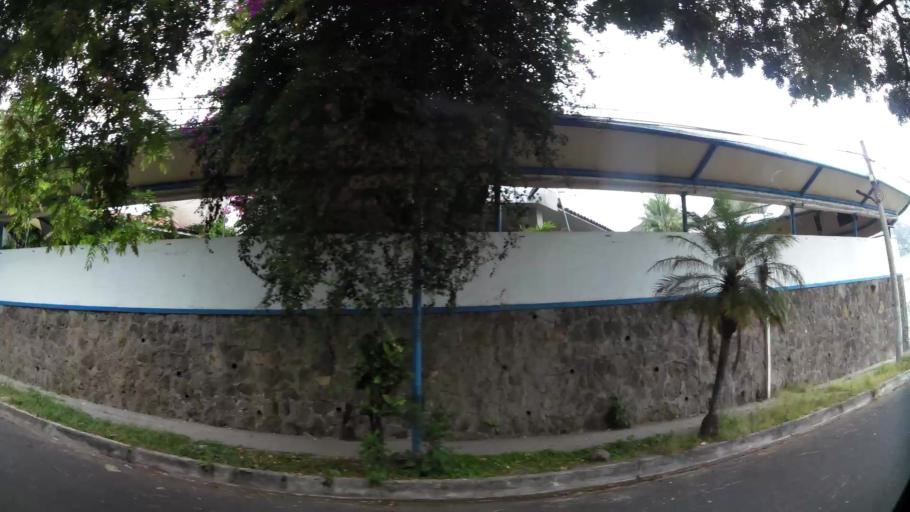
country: SV
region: San Salvador
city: Mejicanos
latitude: 13.7076
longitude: -89.2385
